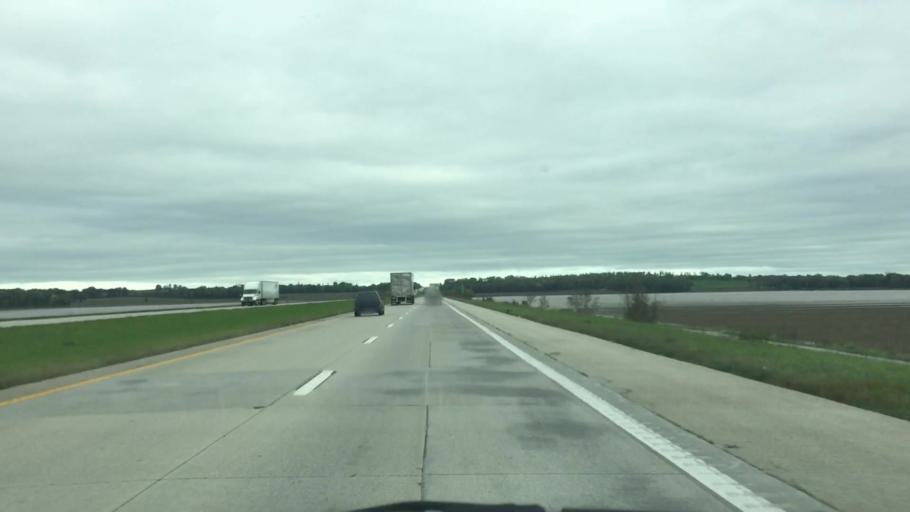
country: US
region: Missouri
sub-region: Daviess County
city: Gallatin
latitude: 40.0340
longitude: -94.0951
